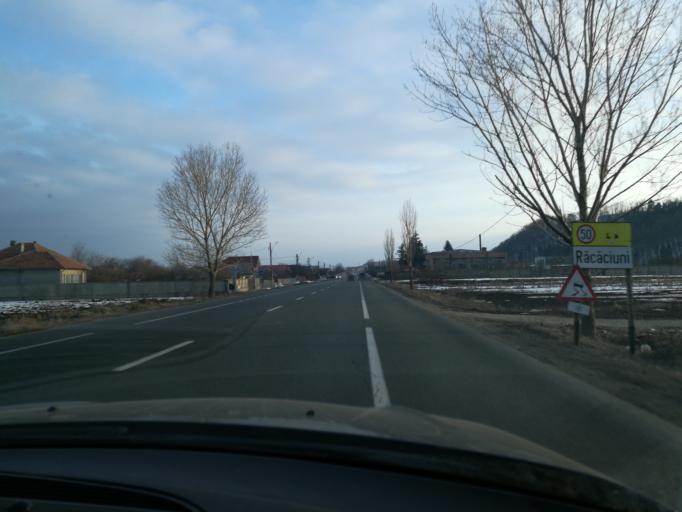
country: RO
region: Bacau
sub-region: Comuna Racaciuni
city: Racaciuni
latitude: 46.3435
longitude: 26.9986
